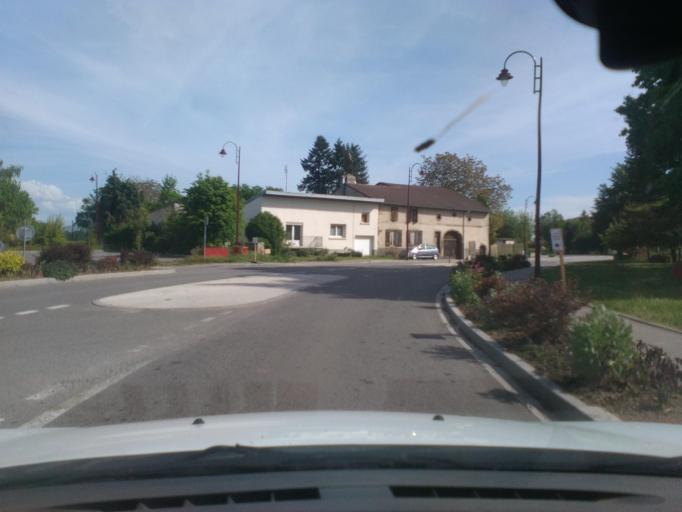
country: FR
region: Lorraine
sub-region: Departement des Vosges
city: Rambervillers
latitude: 48.3846
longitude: 6.6043
